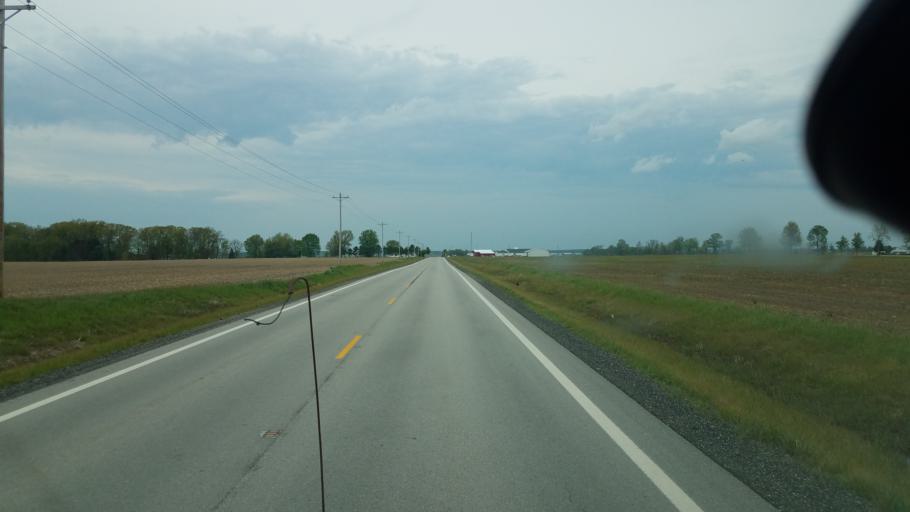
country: US
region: Ohio
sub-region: Huron County
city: Plymouth
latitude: 40.9761
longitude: -82.7434
